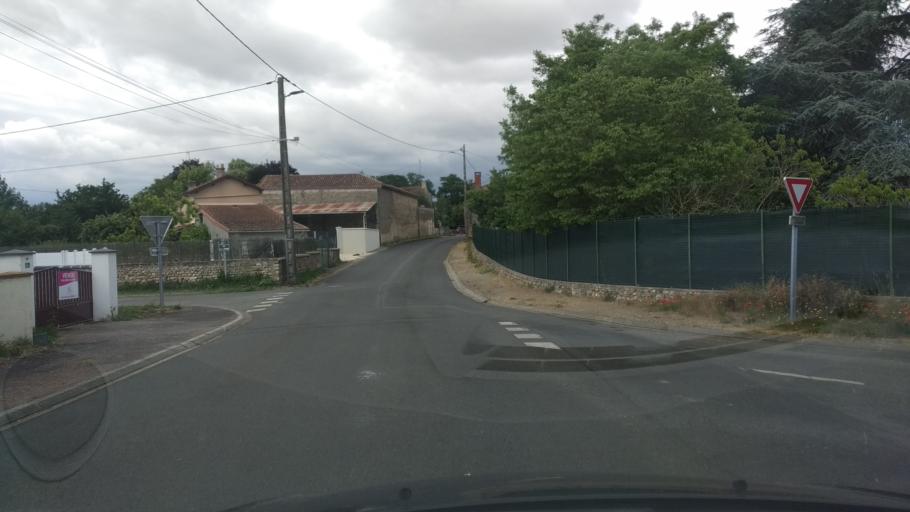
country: FR
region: Poitou-Charentes
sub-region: Departement de la Vienne
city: Vouille
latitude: 46.6301
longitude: 0.1867
